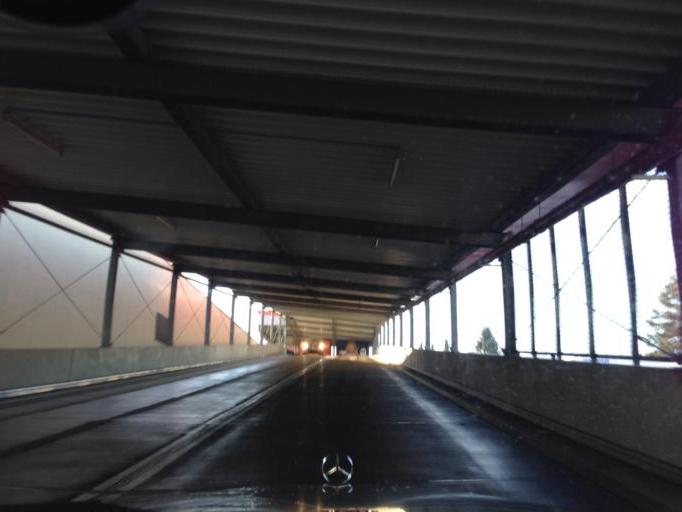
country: DE
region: Hamburg
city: Steilshoop
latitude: 53.6131
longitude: 10.0790
